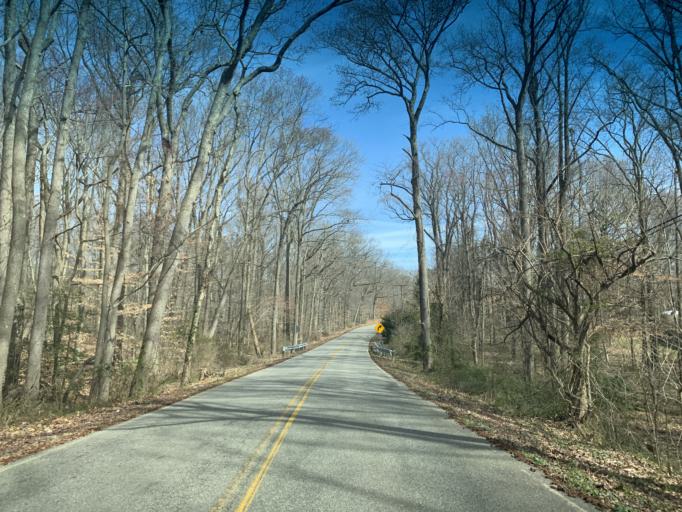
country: US
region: Maryland
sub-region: Cecil County
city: Charlestown
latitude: 39.5588
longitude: -76.0111
